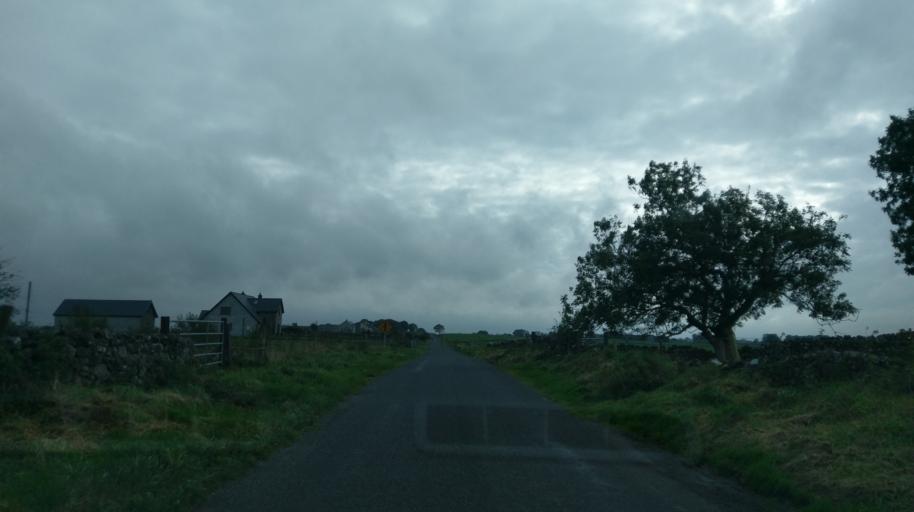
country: IE
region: Connaught
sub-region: County Galway
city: Athenry
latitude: 53.4607
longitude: -8.6225
